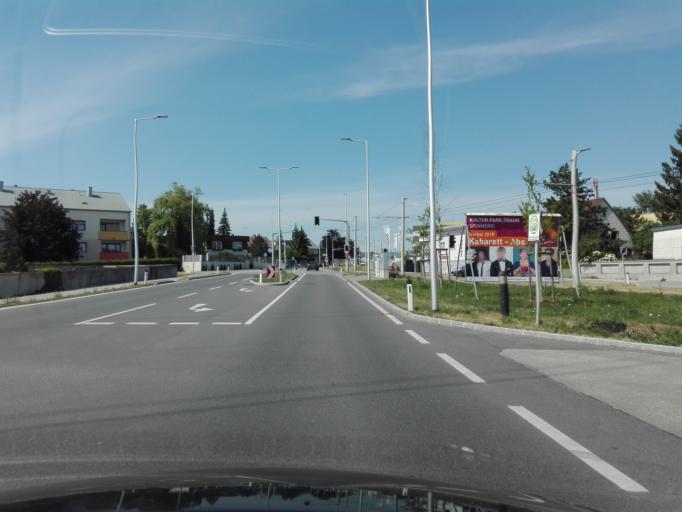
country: AT
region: Upper Austria
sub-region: Politischer Bezirk Linz-Land
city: Traun
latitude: 48.2279
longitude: 14.2338
